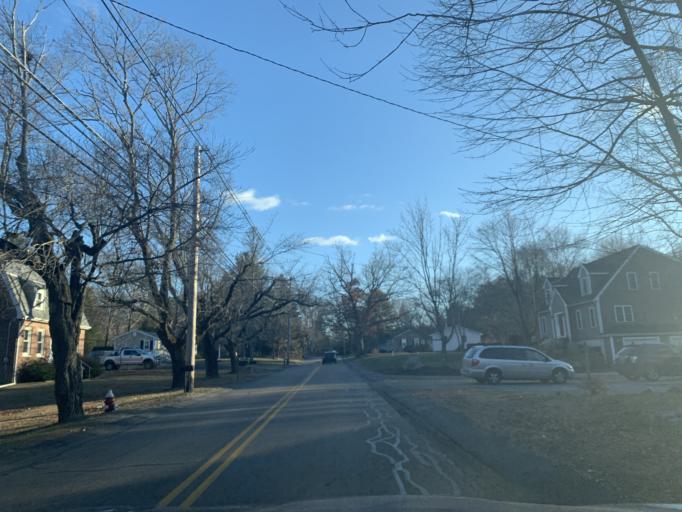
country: US
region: Massachusetts
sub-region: Bristol County
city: Norton
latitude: 41.9421
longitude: -71.2026
